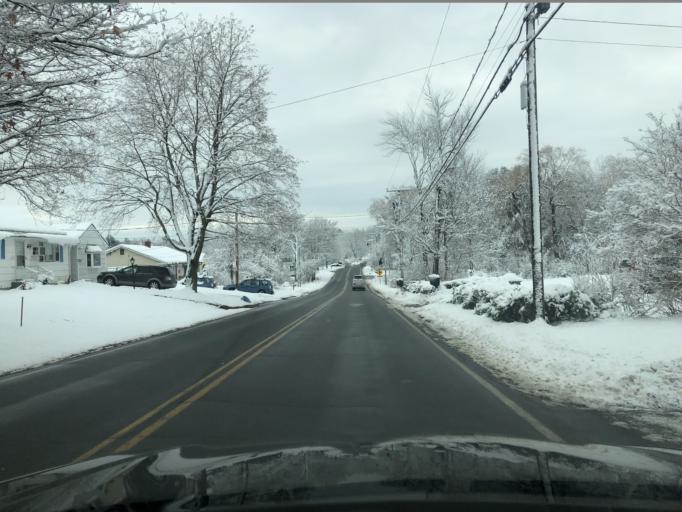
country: US
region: New Hampshire
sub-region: Strafford County
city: Somersworth
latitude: 43.2429
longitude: -70.8626
